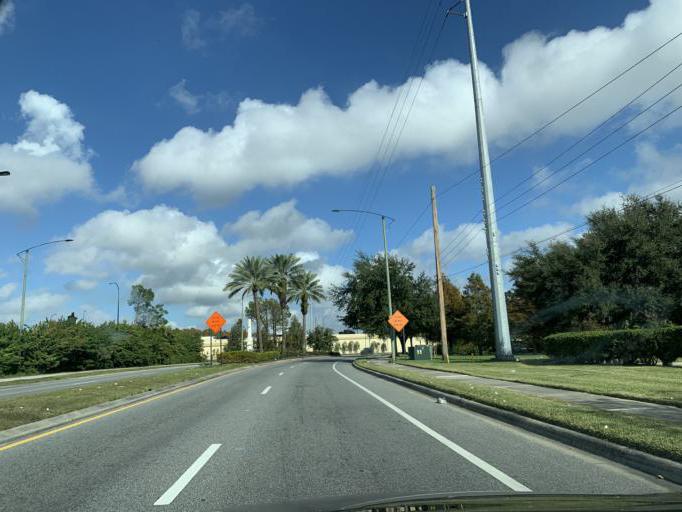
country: US
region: Florida
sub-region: Orange County
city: Oak Ridge
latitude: 28.4827
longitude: -81.4423
